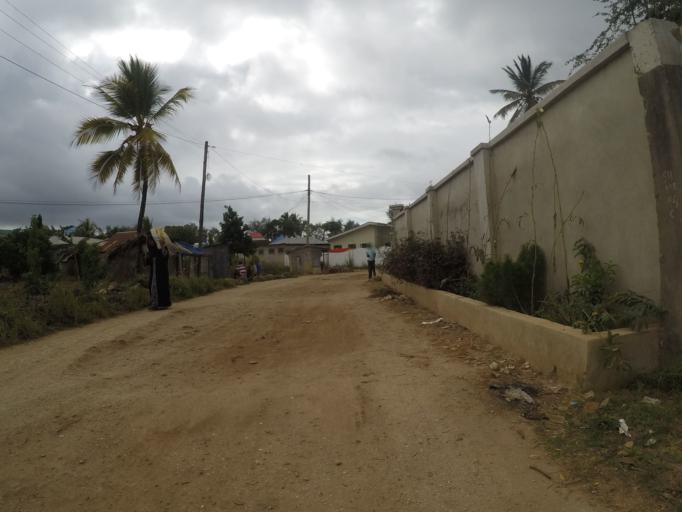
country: TZ
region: Zanzibar Urban/West
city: Zanzibar
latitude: -6.2144
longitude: 39.2169
